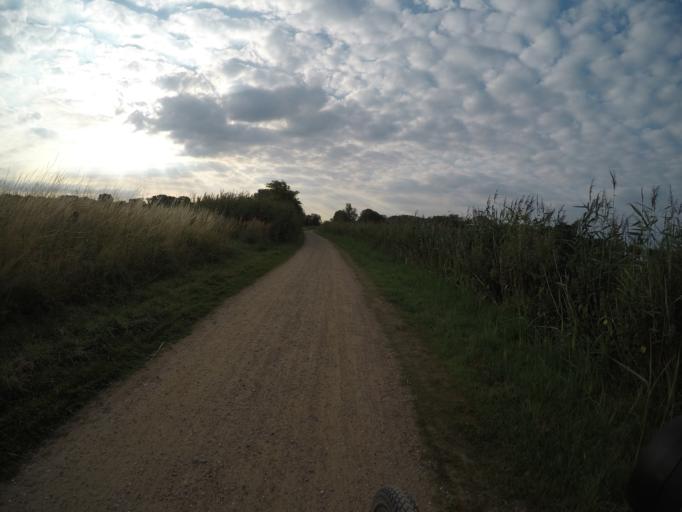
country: DE
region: Schleswig-Holstein
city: Oststeinbek
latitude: 53.5026
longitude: 10.1440
